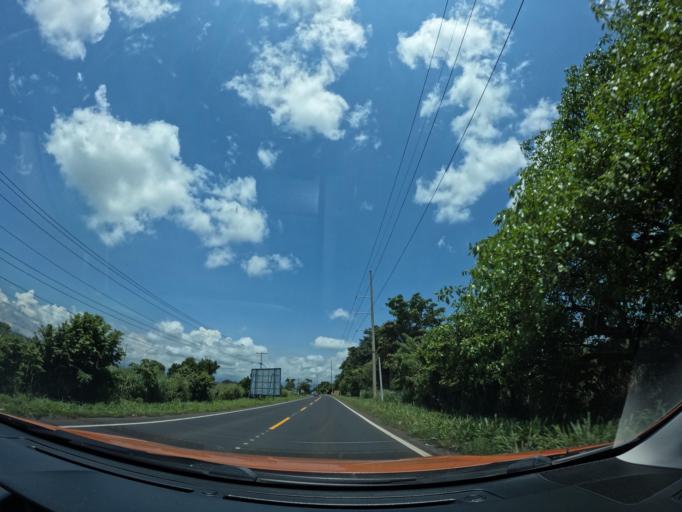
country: GT
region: Escuintla
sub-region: Municipio de Masagua
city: Masagua
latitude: 14.2398
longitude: -90.8167
